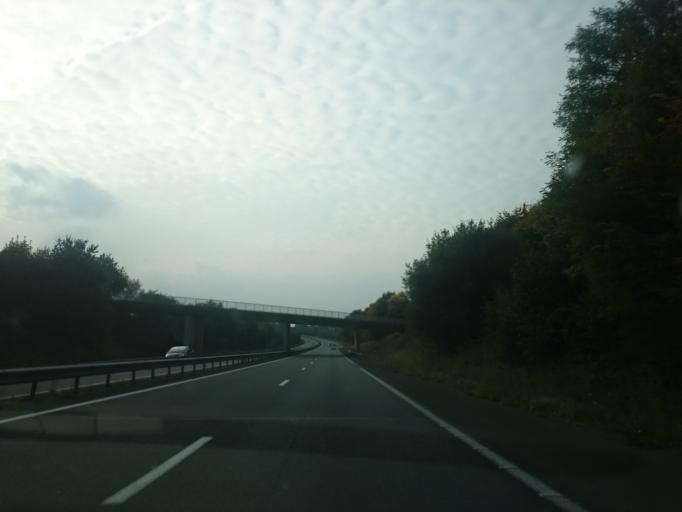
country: FR
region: Brittany
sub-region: Departement des Cotes-d'Armor
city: Pedernec
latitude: 48.5712
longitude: -3.2584
